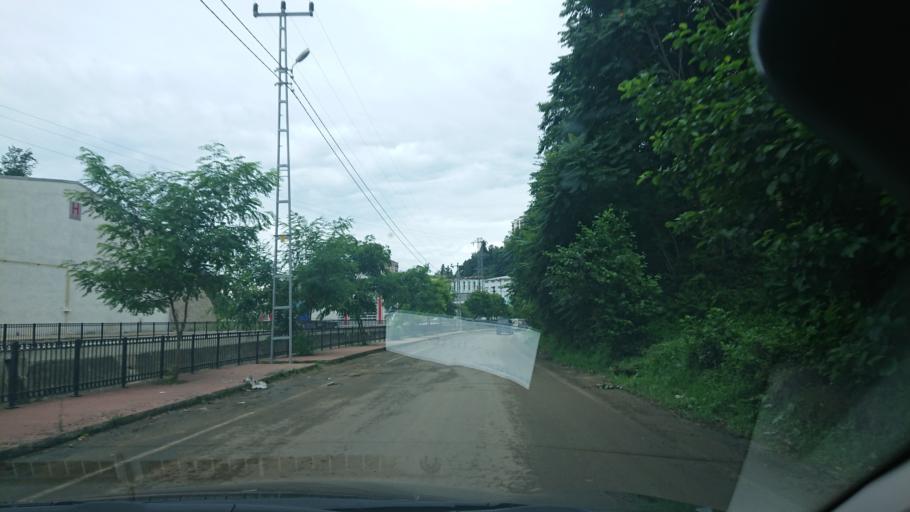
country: TR
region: Rize
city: Rize
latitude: 41.0300
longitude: 40.4830
